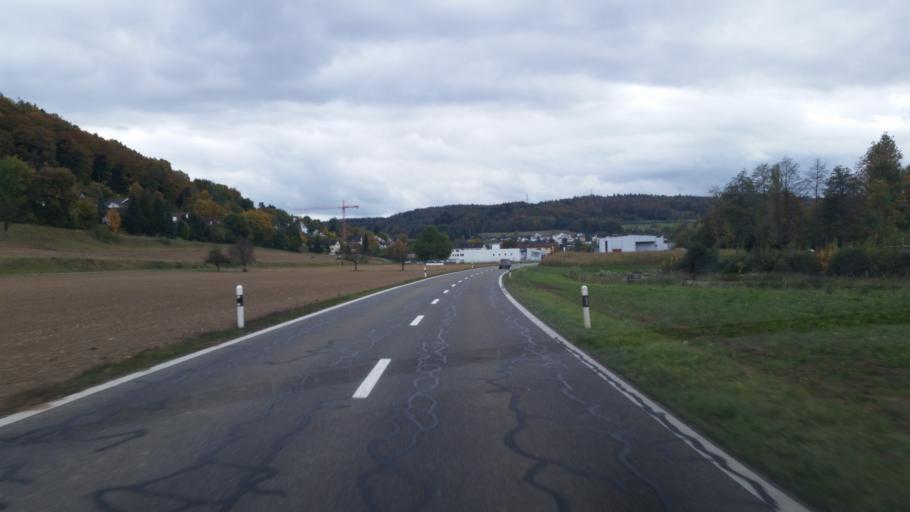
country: CH
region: Aargau
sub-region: Bezirk Zurzach
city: Oberendingen
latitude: 47.5457
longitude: 8.2898
